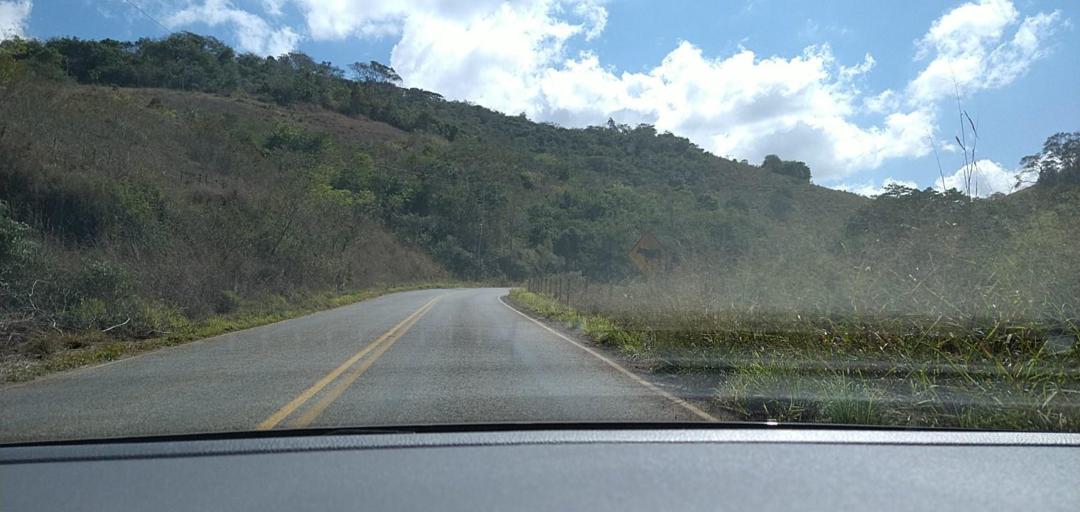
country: BR
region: Minas Gerais
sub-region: Ponte Nova
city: Ponte Nova
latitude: -20.2746
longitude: -42.9027
